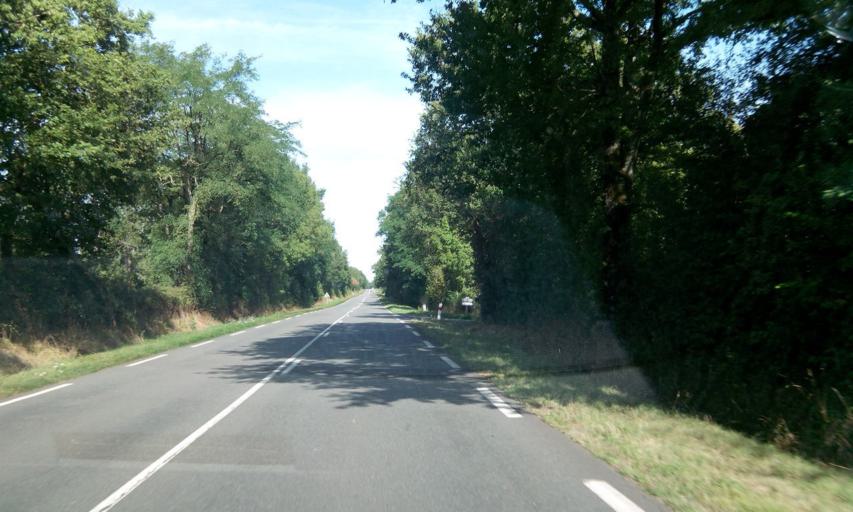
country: FR
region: Poitou-Charentes
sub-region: Departement de la Charente
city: Chabanais
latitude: 45.9463
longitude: 0.7235
